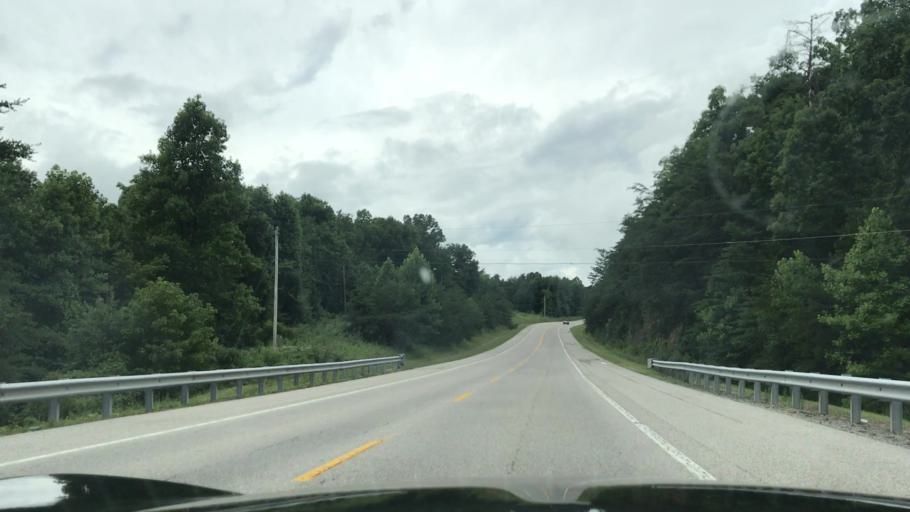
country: US
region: Tennessee
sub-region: Putnam County
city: Monterey
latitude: 36.1341
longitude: -85.1113
